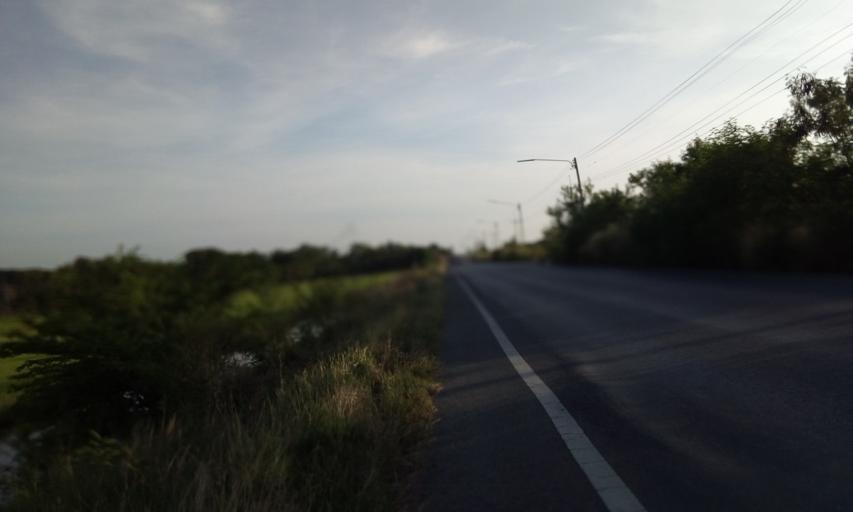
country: TH
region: Pathum Thani
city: Ban Rangsit
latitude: 14.0458
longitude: 100.8446
